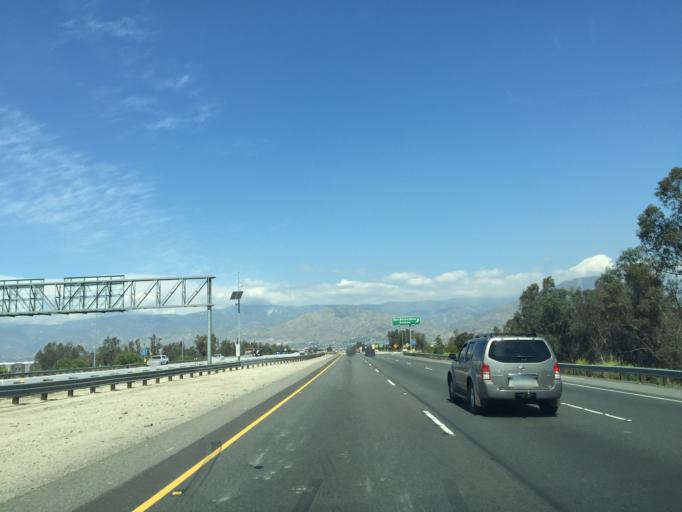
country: US
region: California
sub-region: San Bernardino County
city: Redlands
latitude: 34.0754
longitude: -117.2006
